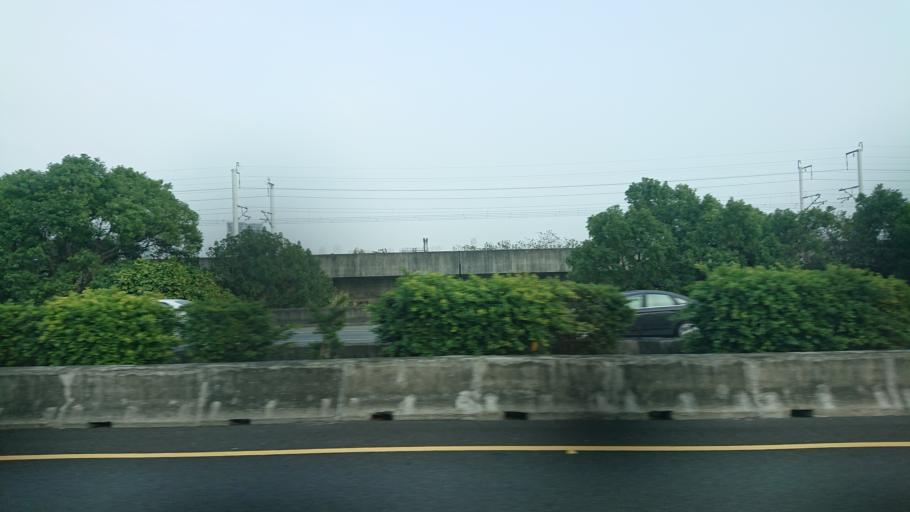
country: TW
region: Taiwan
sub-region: Taichung City
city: Taichung
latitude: 24.1344
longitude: 120.6175
